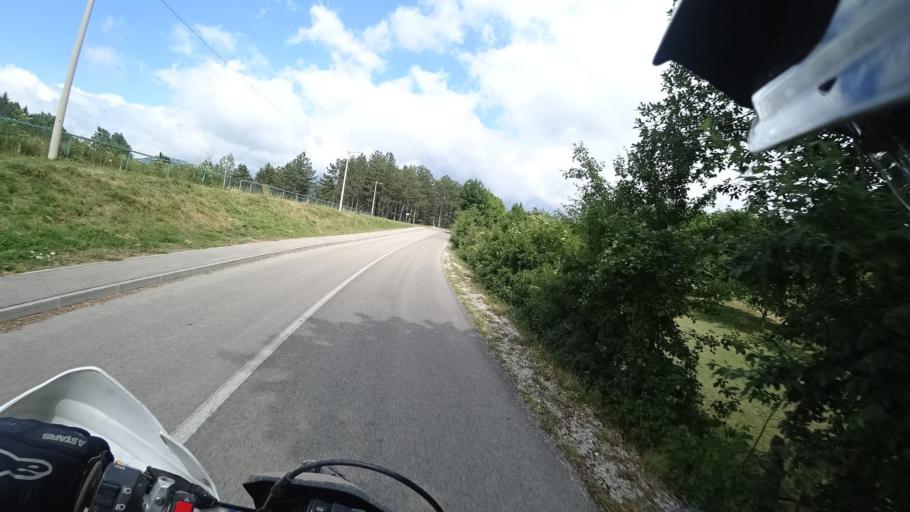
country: HR
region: Zadarska
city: Gracac
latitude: 44.5304
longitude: 15.7722
